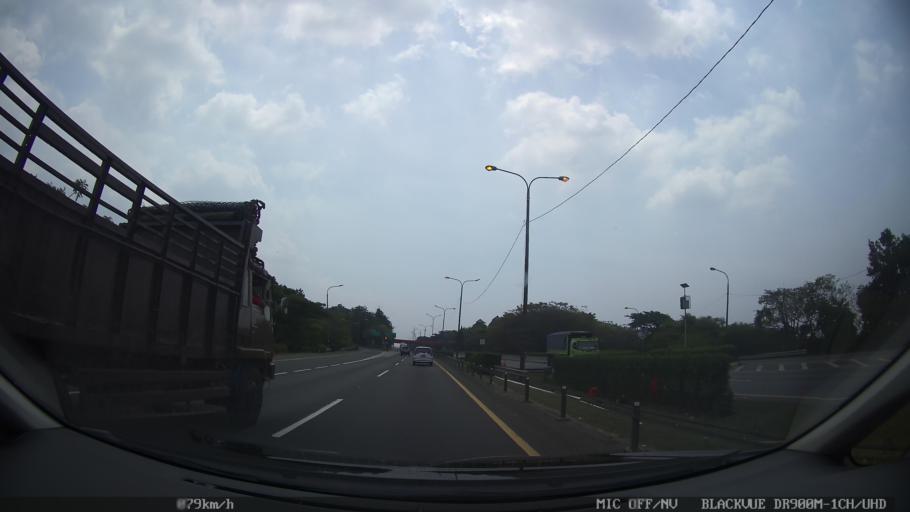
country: ID
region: Banten
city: Serang
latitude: -6.1167
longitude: 106.1871
